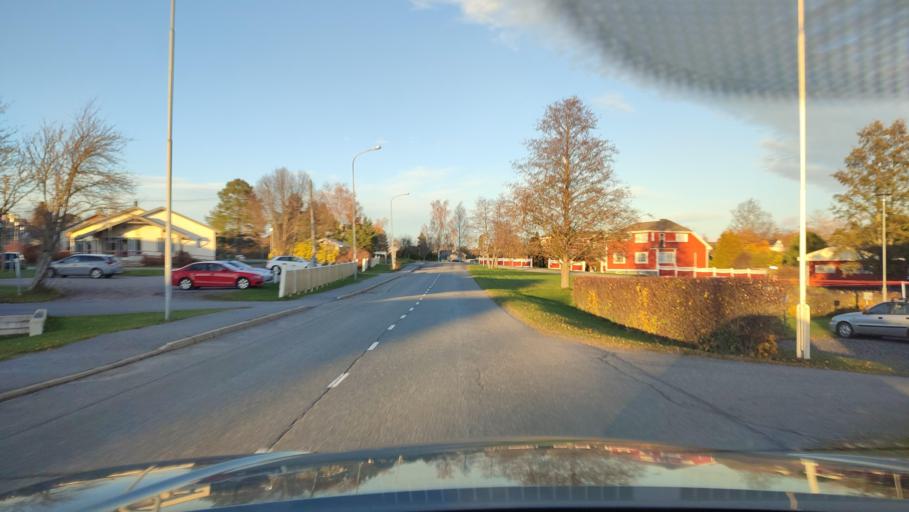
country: FI
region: Ostrobothnia
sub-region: Sydosterbotten
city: Kristinestad
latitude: 62.2680
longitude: 21.3716
